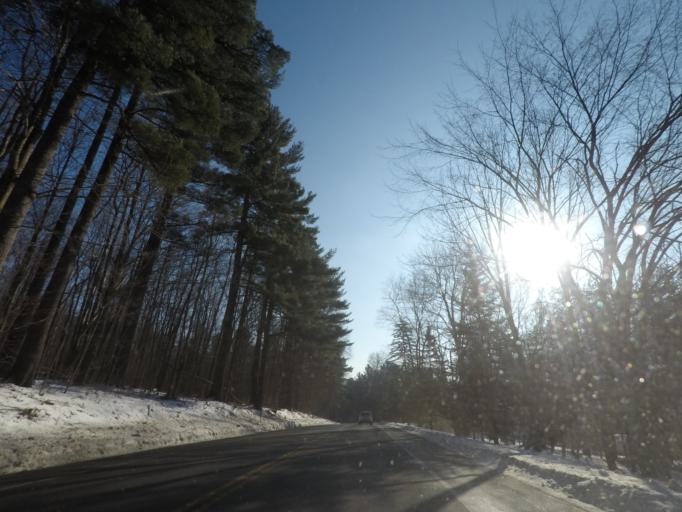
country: US
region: Massachusetts
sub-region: Berkshire County
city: Richmond
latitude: 42.4849
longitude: -73.3738
